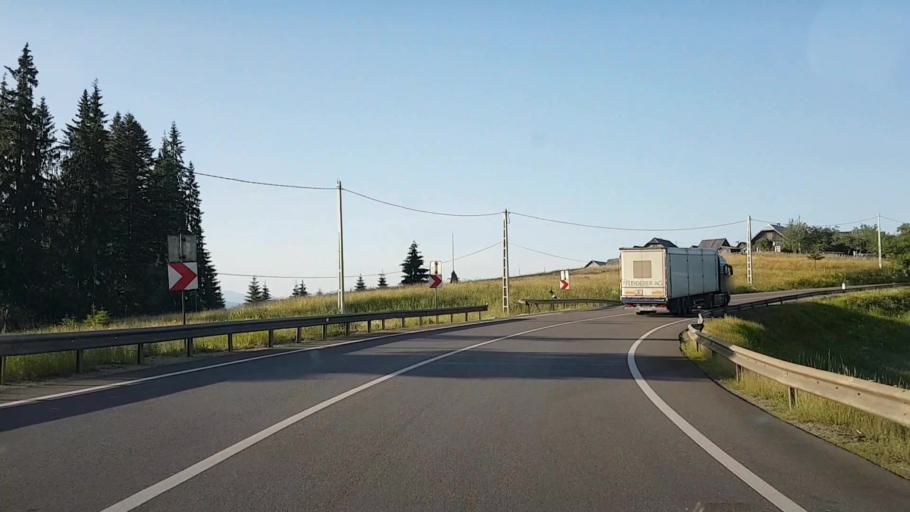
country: RO
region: Suceava
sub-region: Comuna Poiana Stampei
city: Poiana Stampei
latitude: 47.2914
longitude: 25.0768
